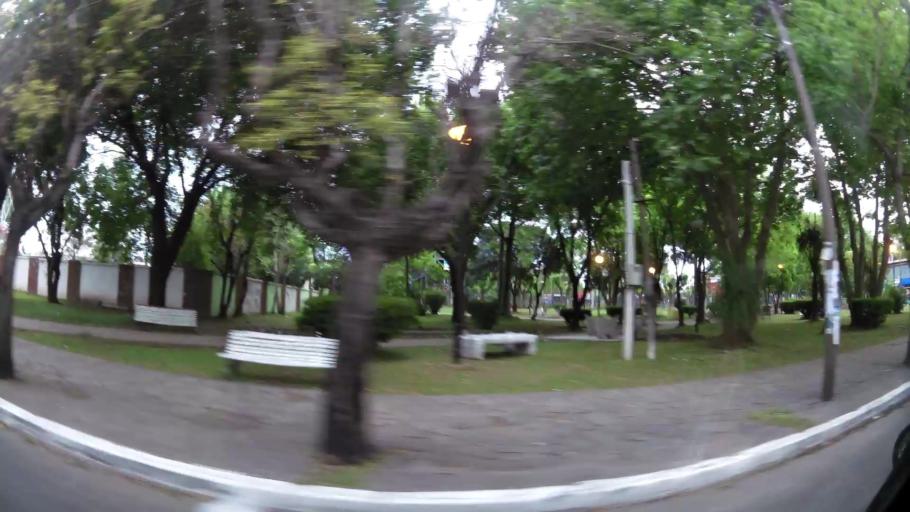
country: AR
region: Buenos Aires
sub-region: Partido de Quilmes
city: Quilmes
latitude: -34.7513
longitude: -58.2342
